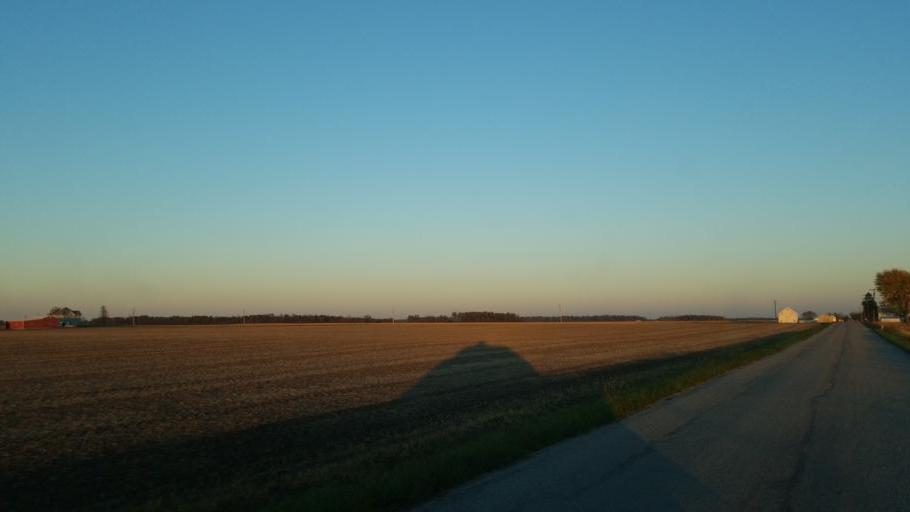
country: US
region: Ohio
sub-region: Huron County
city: Bellevue
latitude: 41.1439
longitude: -82.8294
